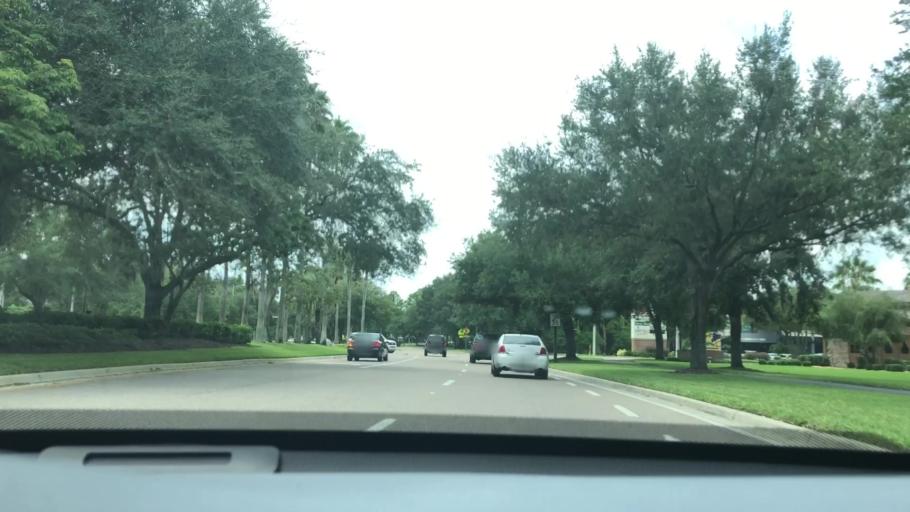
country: US
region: Florida
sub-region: Hillsborough County
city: Pebble Creek
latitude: 28.1169
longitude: -82.3808
